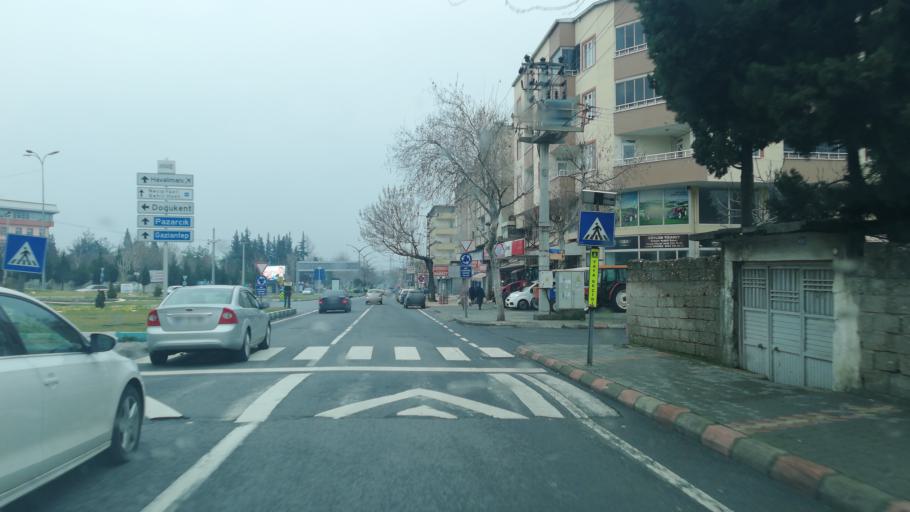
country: TR
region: Kahramanmaras
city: Kahramanmaras
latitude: 37.5670
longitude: 36.9488
